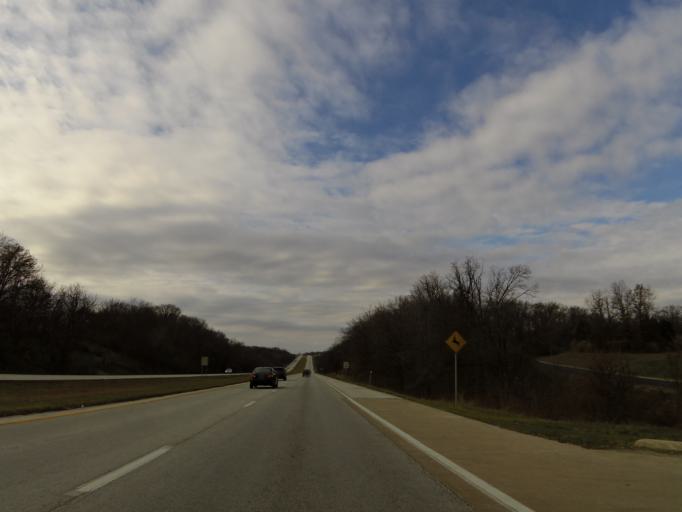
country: US
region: Missouri
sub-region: Marion County
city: Hannibal
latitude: 39.7339
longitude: -91.4050
